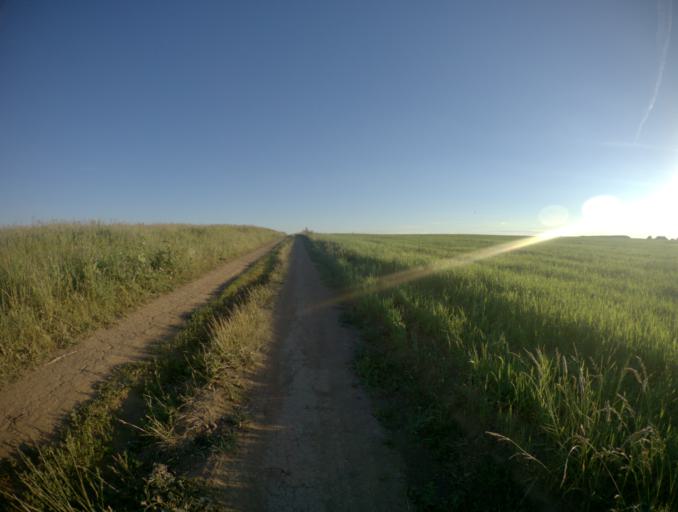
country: RU
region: Vladimir
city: Bogolyubovo
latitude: 56.2066
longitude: 40.5105
